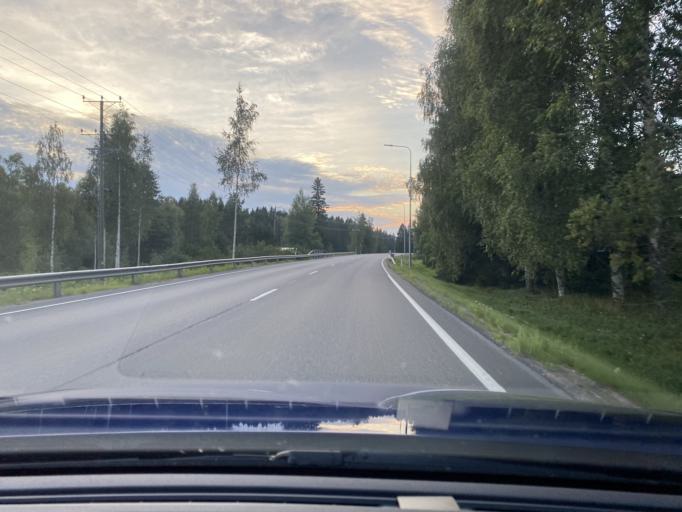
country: FI
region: Satakunta
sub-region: Pohjois-Satakunta
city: Kankaanpaeae
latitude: 61.8055
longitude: 22.3834
